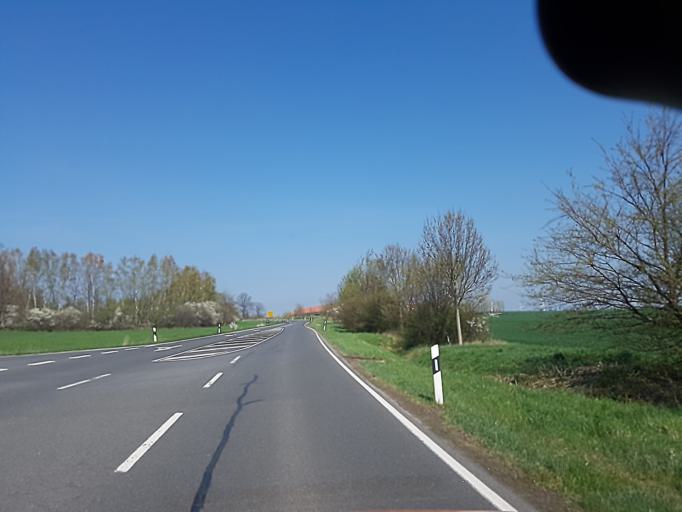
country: DE
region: Saxony
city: Ostrau
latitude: 51.2014
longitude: 12.8913
